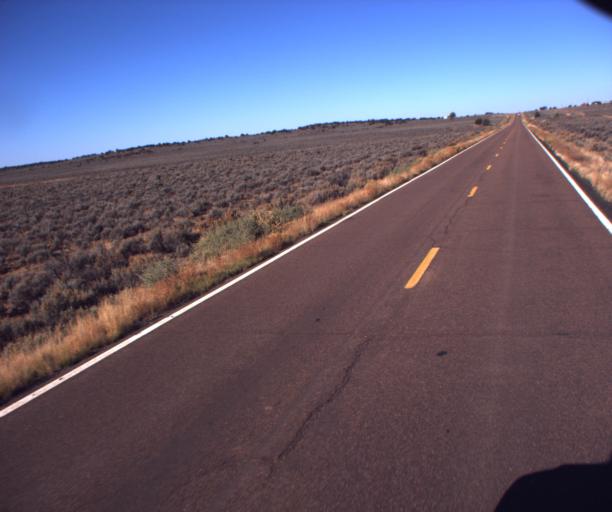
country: US
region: Arizona
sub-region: Apache County
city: Ganado
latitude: 35.7547
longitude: -109.9511
